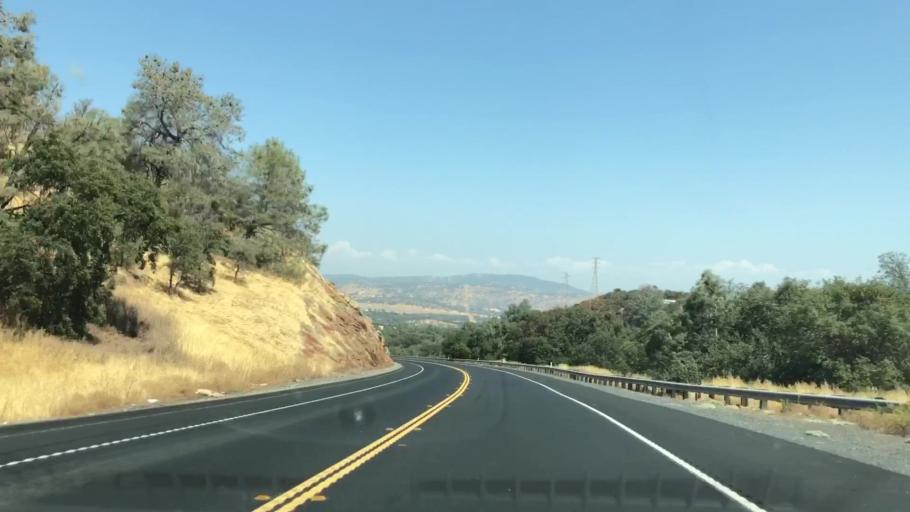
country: US
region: California
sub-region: Calaveras County
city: Copperopolis
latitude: 37.9449
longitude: -120.7002
